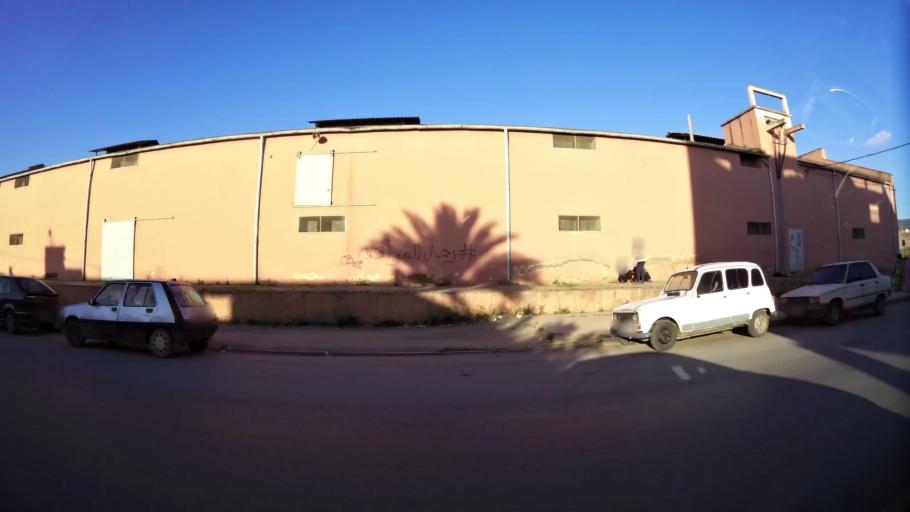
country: MA
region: Oriental
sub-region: Berkane-Taourirt
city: Berkane
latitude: 34.9267
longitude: -2.3184
